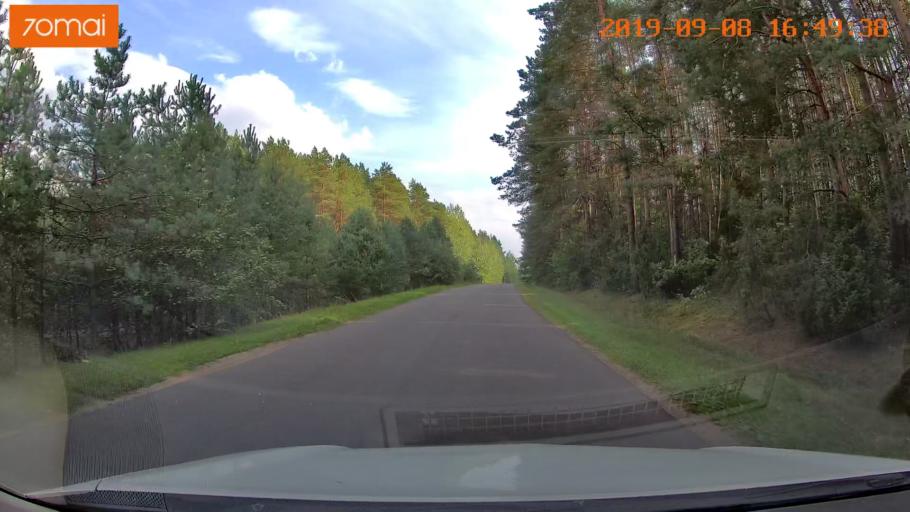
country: BY
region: Grodnenskaya
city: Hrodna
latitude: 53.8086
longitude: 23.8771
